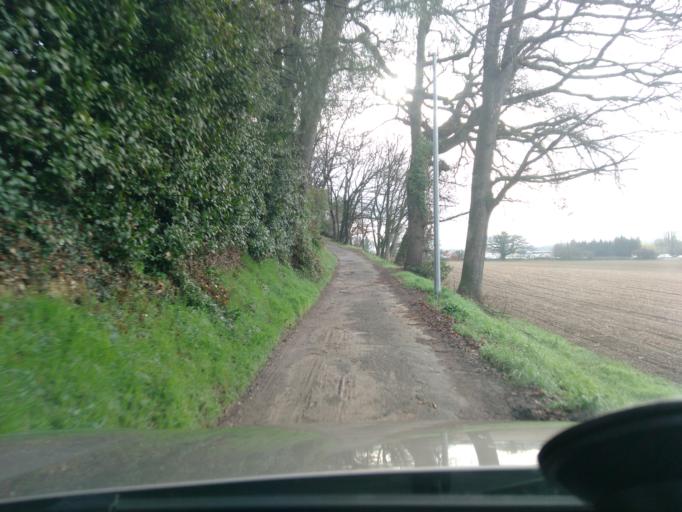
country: FR
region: Rhone-Alpes
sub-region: Departement de la Drome
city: Montboucher-sur-Jabron
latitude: 44.5509
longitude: 4.7872
